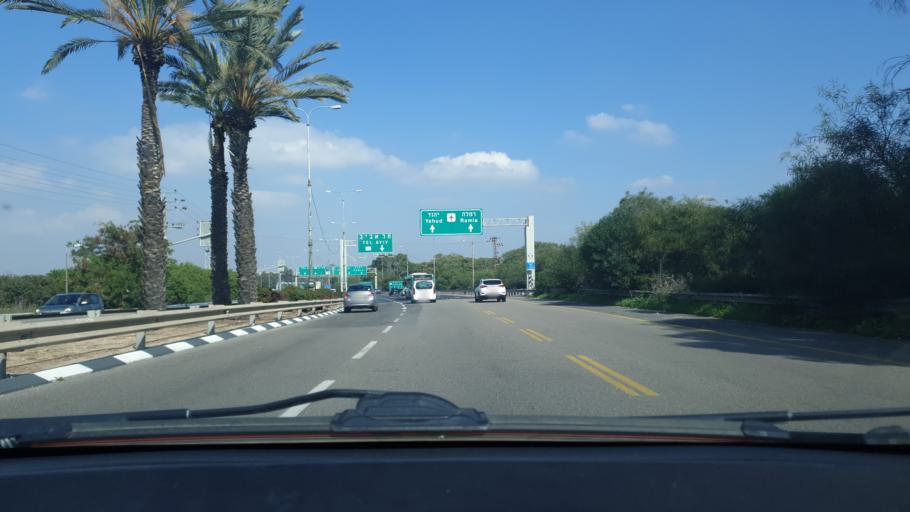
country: IL
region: Central District
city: Bet Dagan
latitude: 31.9968
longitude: 34.8178
